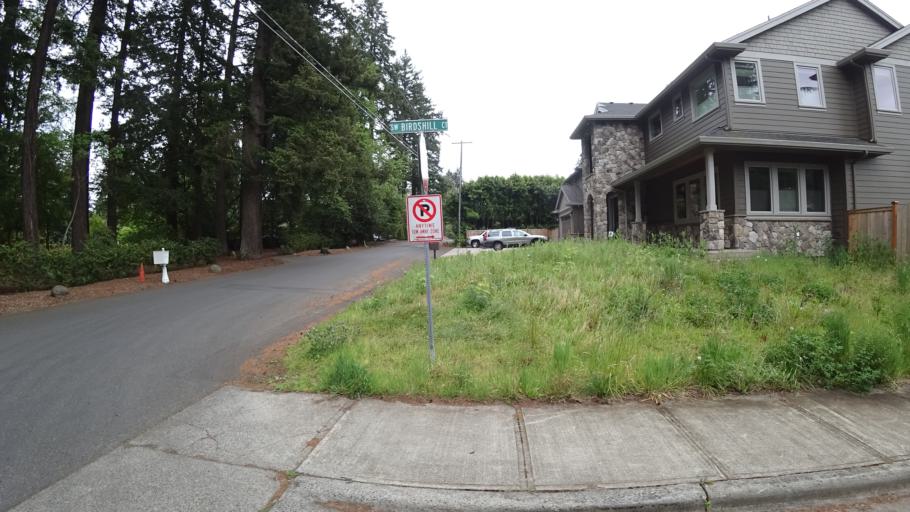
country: US
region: Oregon
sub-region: Washington County
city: Garden Home-Whitford
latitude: 45.4683
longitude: -122.7580
